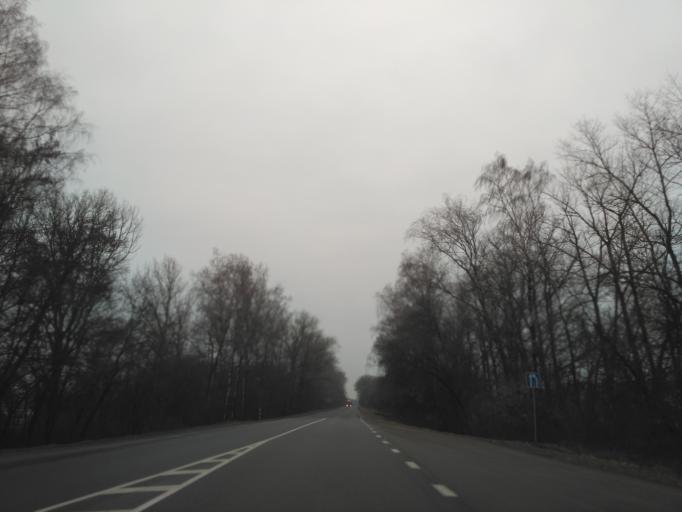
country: BY
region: Brest
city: Baranovichi
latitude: 53.1914
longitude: 26.0851
